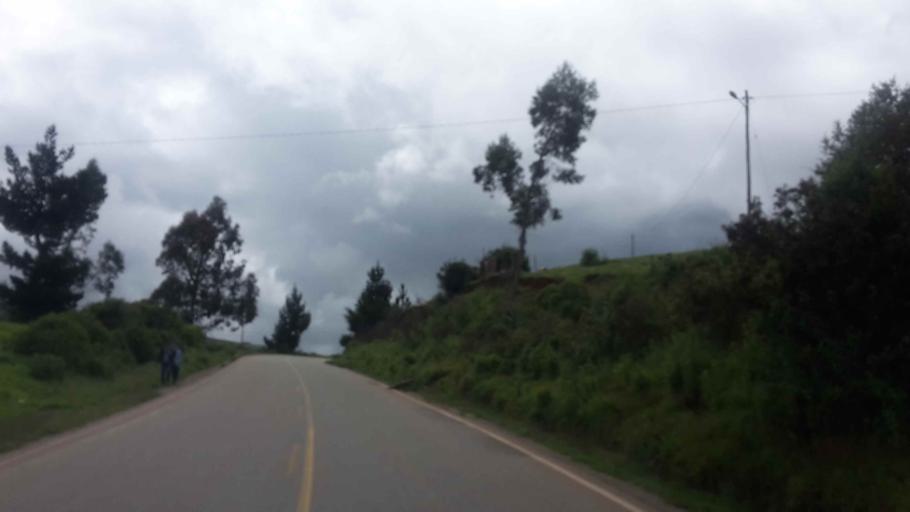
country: BO
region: Cochabamba
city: Totora
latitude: -17.5634
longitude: -65.3369
